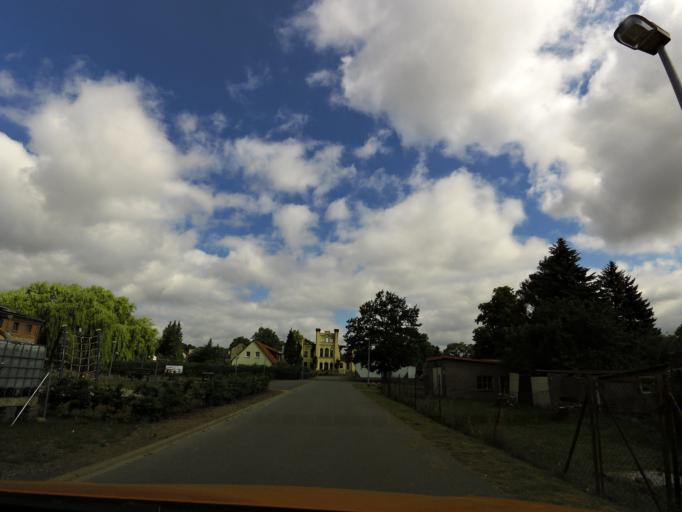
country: DE
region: Mecklenburg-Vorpommern
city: Krakow am See
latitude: 53.6848
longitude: 12.2676
